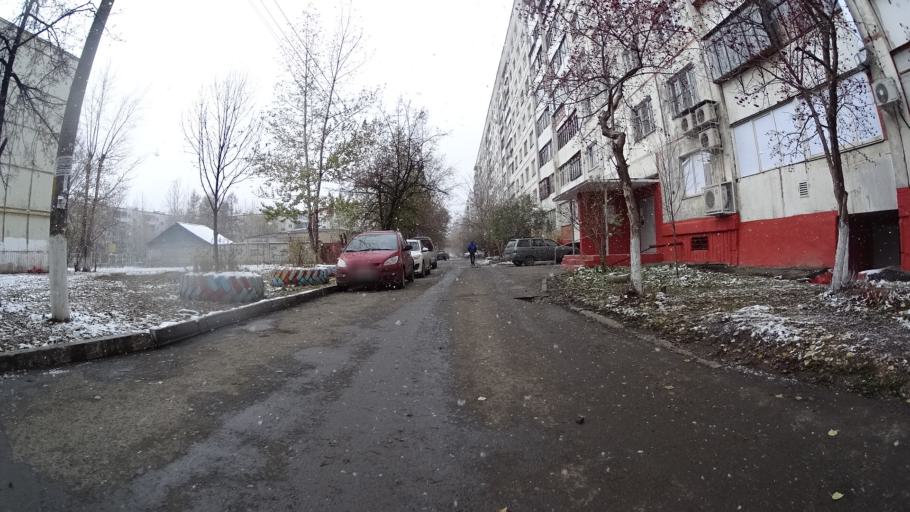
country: RU
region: Chelyabinsk
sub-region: Gorod Chelyabinsk
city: Chelyabinsk
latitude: 55.1939
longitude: 61.3131
